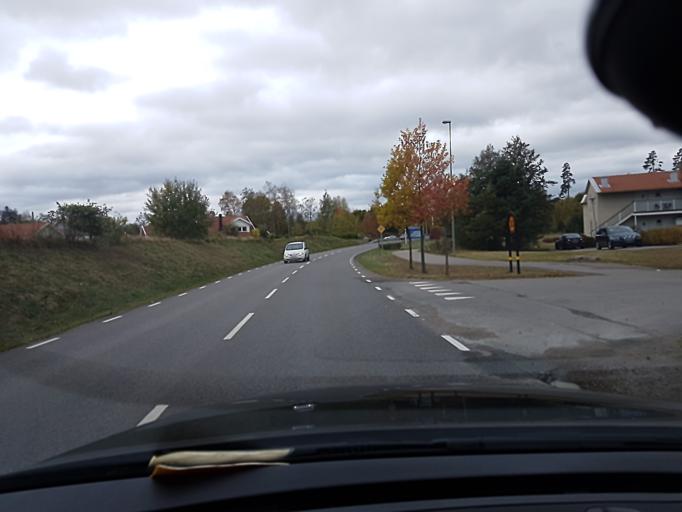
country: SE
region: Kronoberg
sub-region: Vaxjo Kommun
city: Vaexjoe
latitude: 56.9135
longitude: 14.8022
